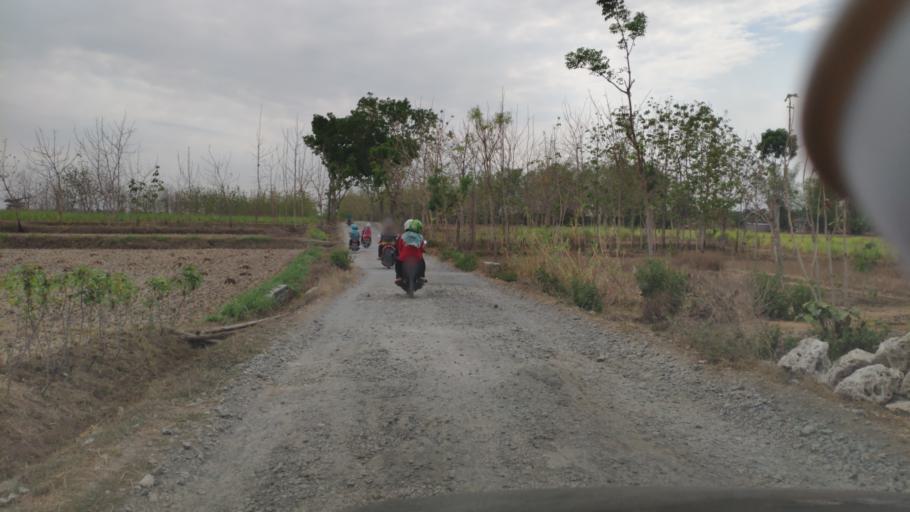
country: ID
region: Central Java
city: Jembangan
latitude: -6.9521
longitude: 111.3847
